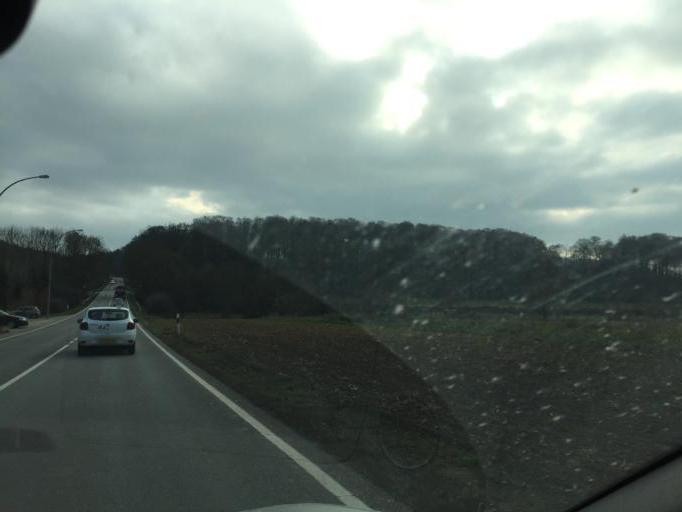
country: LU
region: Diekirch
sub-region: Canton de Redange
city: Saeul
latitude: 49.7471
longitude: 5.9744
